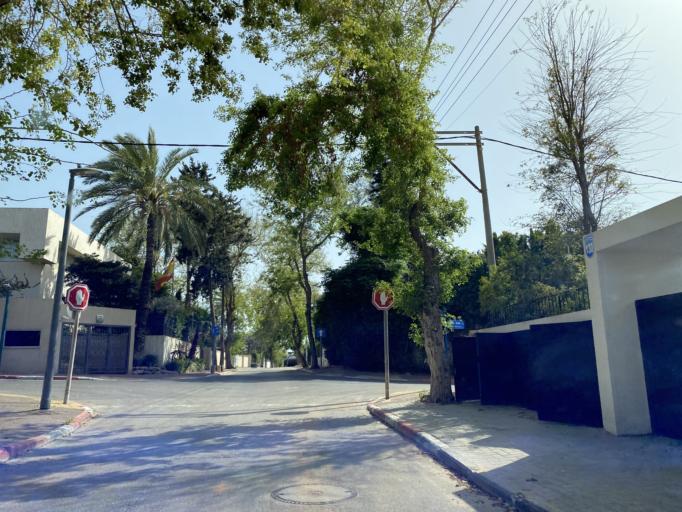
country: IL
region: Tel Aviv
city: Herzliya Pituah
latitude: 32.1762
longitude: 34.8070
